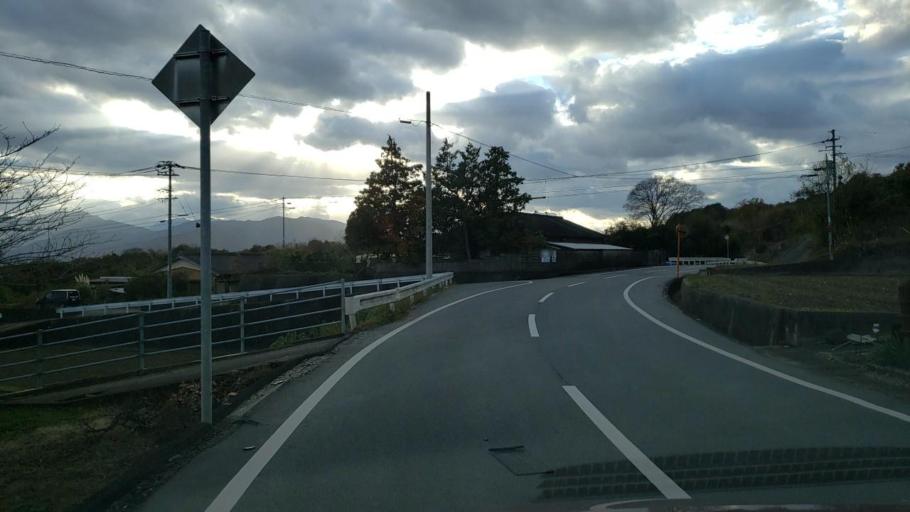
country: JP
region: Tokushima
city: Wakimachi
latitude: 34.0900
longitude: 134.2015
